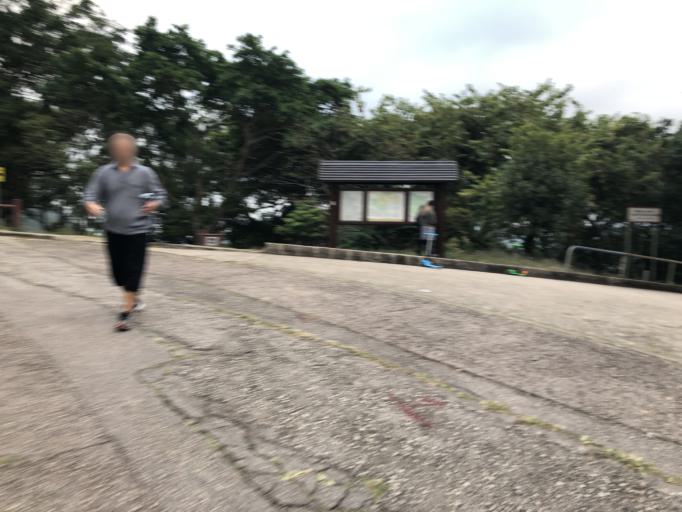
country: HK
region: Wanchai
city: Wan Chai
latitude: 22.2669
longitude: 114.2134
